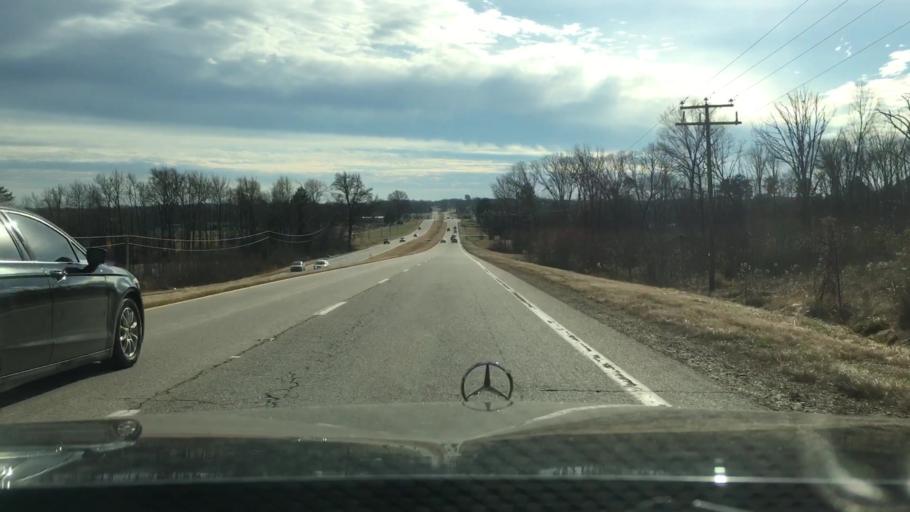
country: US
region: Virginia
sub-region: Pittsylvania County
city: Mount Hermon
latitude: 36.7417
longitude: -79.3788
